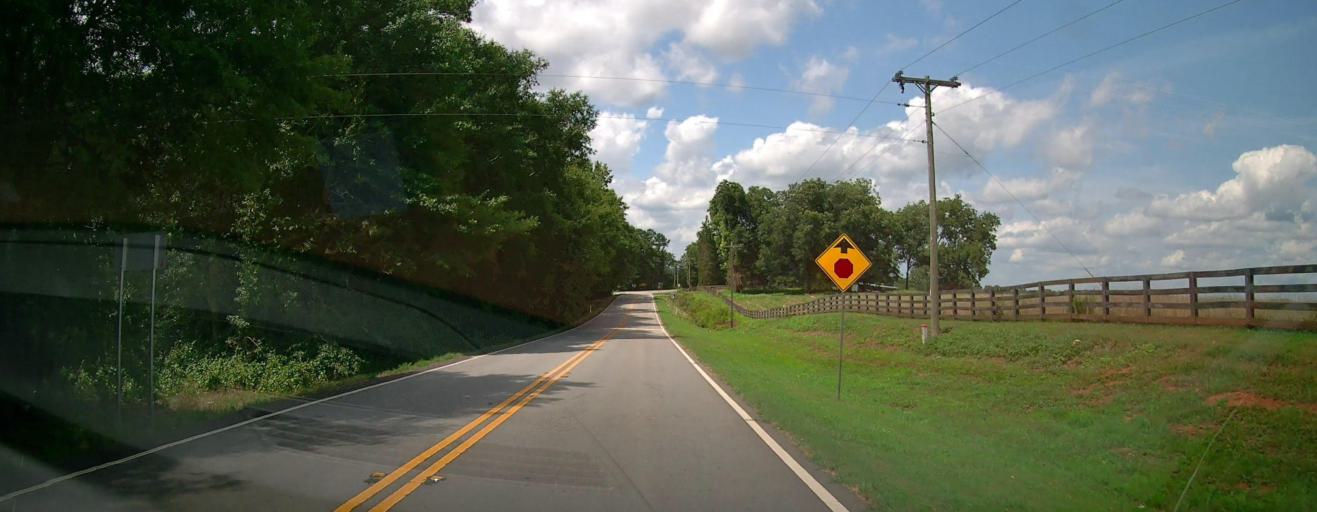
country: US
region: Georgia
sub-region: Carroll County
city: Bowdon
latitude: 33.4673
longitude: -85.2953
